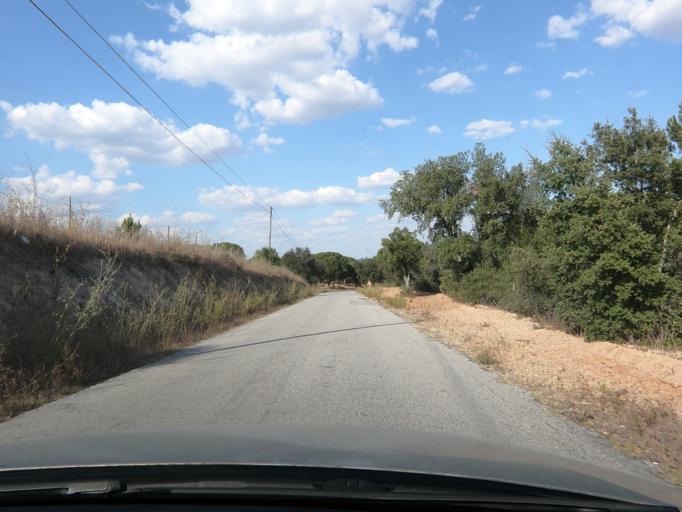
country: PT
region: Setubal
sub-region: Alcacer do Sal
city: Alcacer do Sal
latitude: 38.2434
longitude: -8.3639
